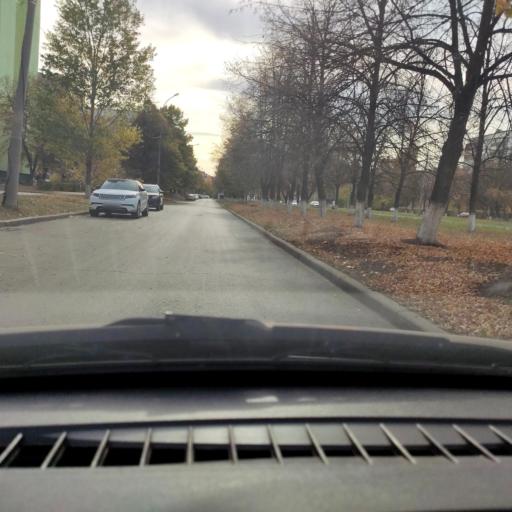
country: RU
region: Samara
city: Tol'yatti
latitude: 53.5213
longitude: 49.3109
